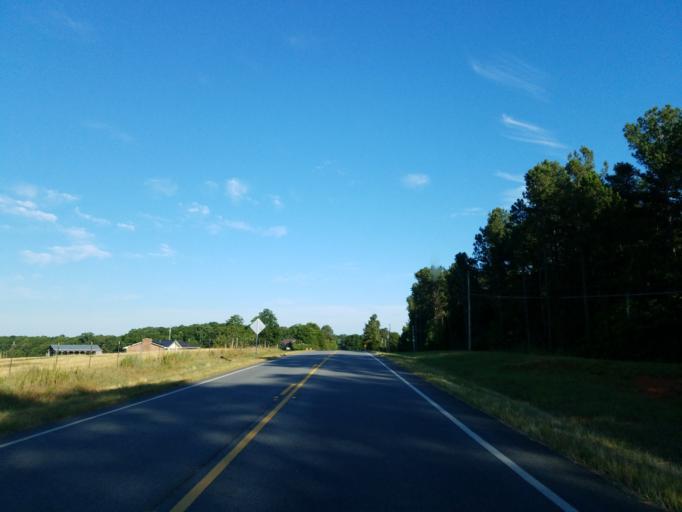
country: US
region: Georgia
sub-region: Gordon County
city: Calhoun
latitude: 34.5523
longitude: -85.0061
